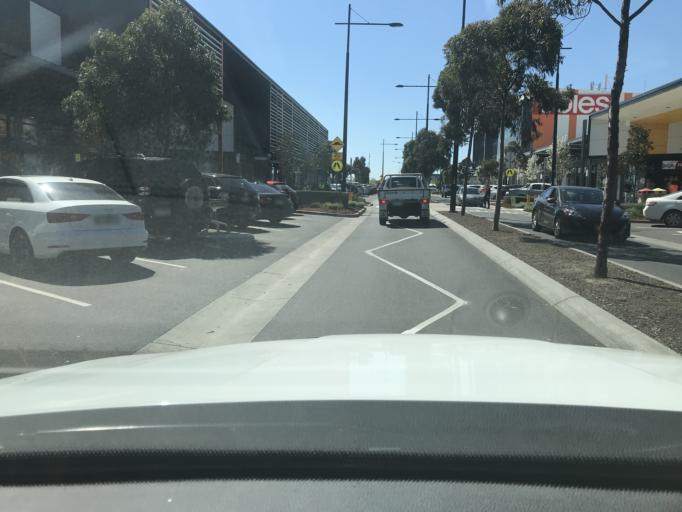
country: AU
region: Victoria
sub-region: Hume
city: Roxburgh Park
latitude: -37.5930
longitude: 144.9142
